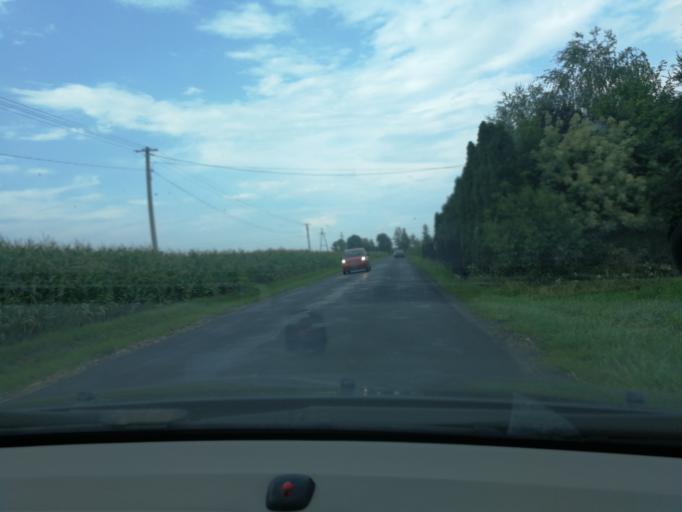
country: PL
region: Masovian Voivodeship
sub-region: Powiat grodziski
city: Grodzisk Mazowiecki
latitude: 52.1284
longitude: 20.5854
